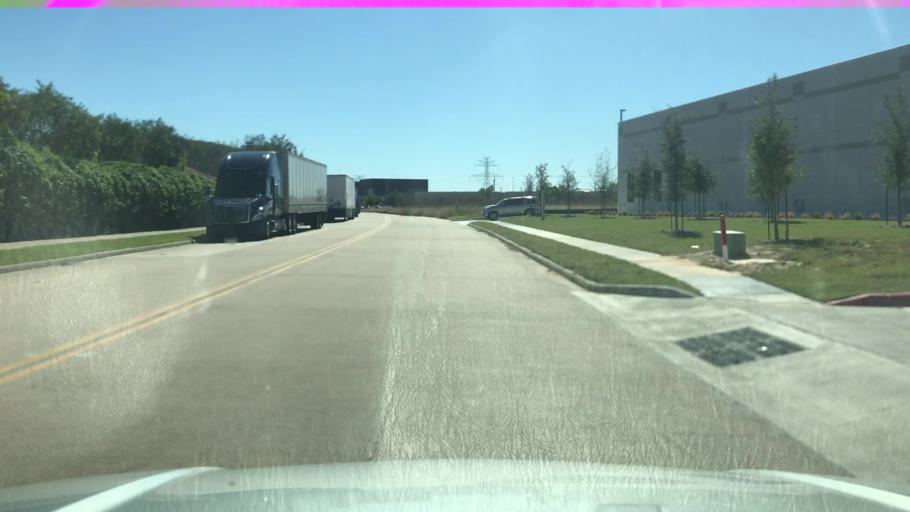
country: US
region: Texas
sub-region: Fort Bend County
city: Cinco Ranch
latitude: 29.7811
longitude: -95.7457
